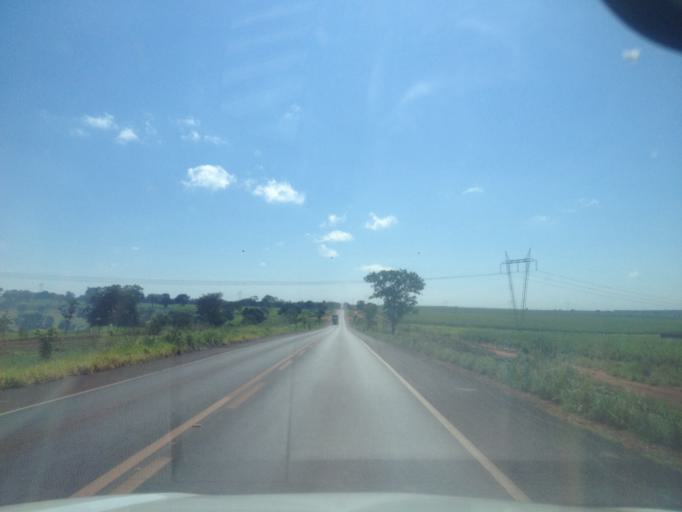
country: BR
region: Minas Gerais
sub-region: Santa Vitoria
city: Santa Vitoria
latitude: -19.0470
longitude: -50.4795
